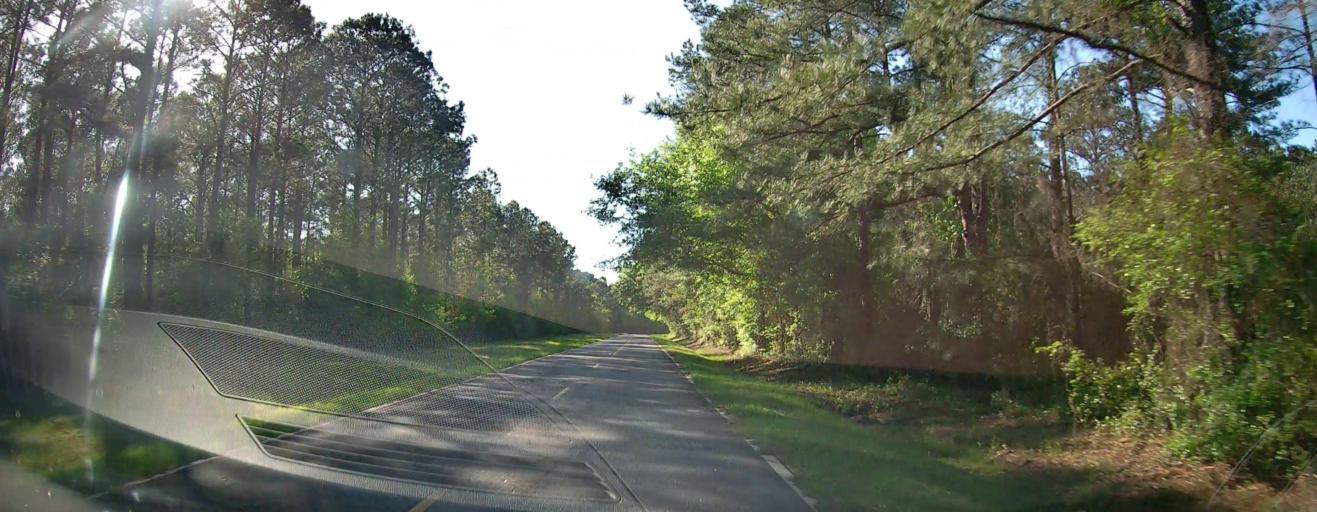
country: US
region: Georgia
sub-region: Houston County
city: Perry
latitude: 32.4709
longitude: -83.7858
